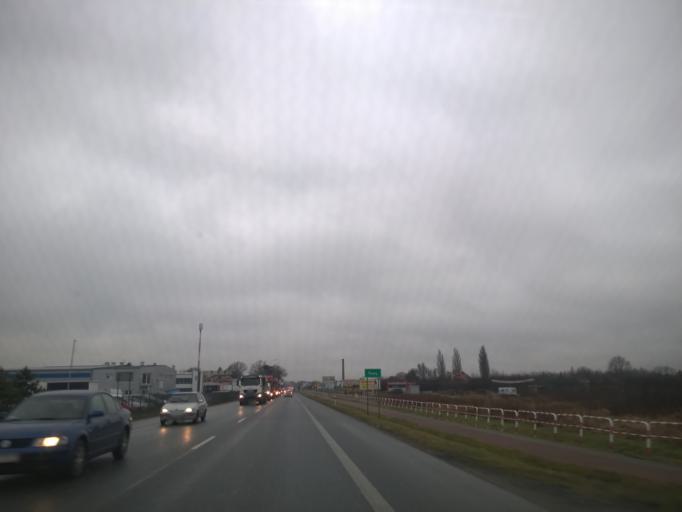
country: PL
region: Lower Silesian Voivodeship
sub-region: Powiat trzebnicki
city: Psary
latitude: 51.1933
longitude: 17.0316
